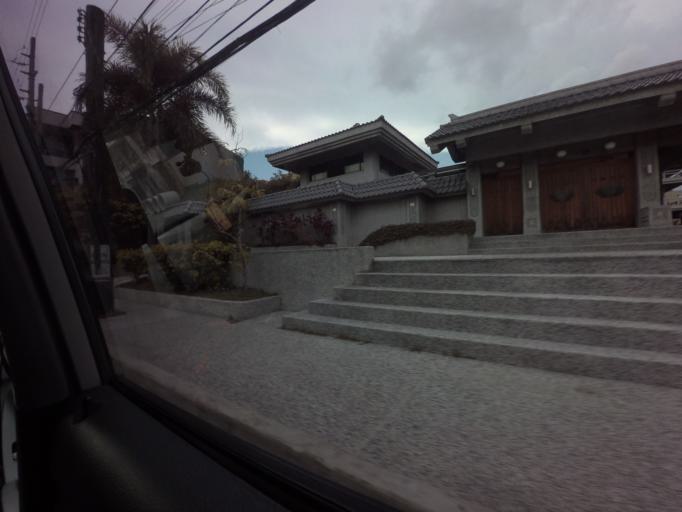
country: PH
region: Calabarzon
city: Del Monte
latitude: 14.6212
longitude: 121.0068
